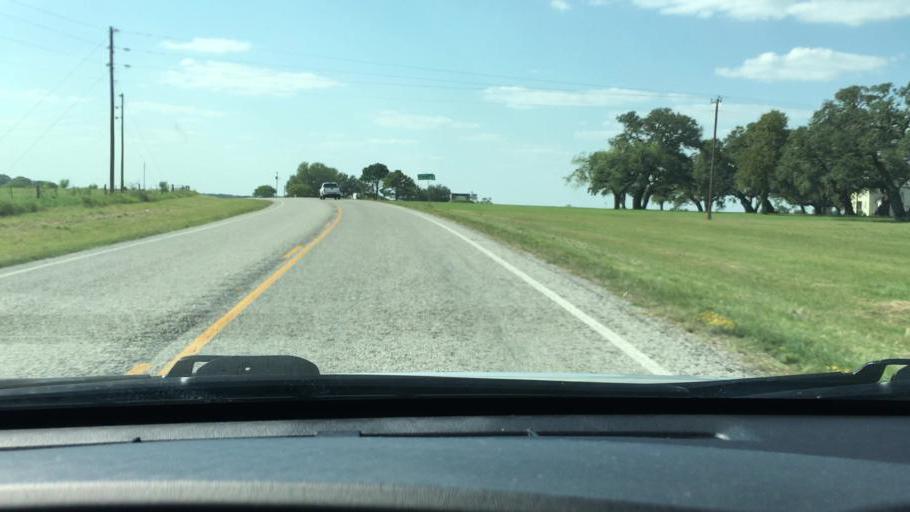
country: US
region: Texas
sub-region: DeWitt County
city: Cuero
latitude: 28.9176
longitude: -97.3286
